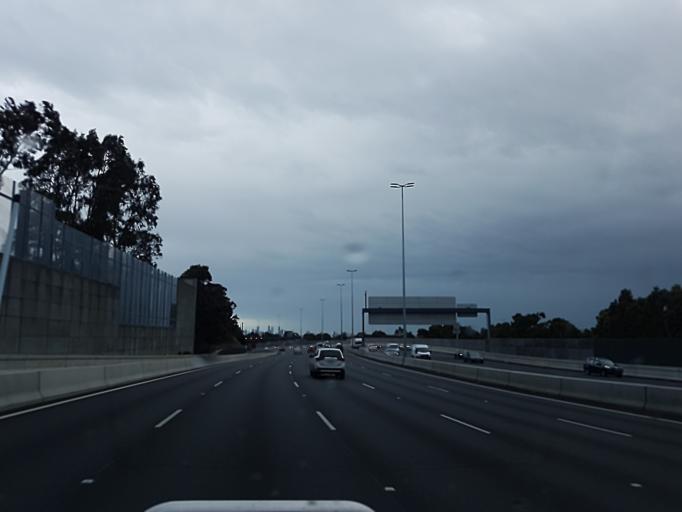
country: AU
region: Victoria
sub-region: Moreland
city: Pascoe Vale
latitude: -37.7380
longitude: 144.9307
